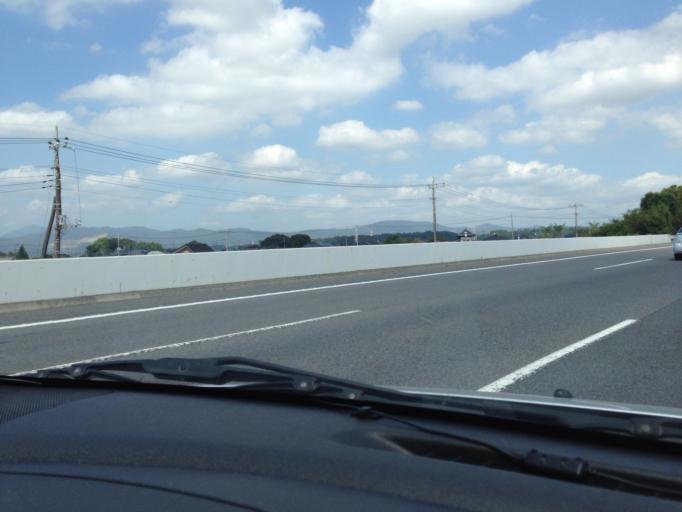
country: JP
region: Ibaraki
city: Naka
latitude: 36.0913
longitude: 140.1606
